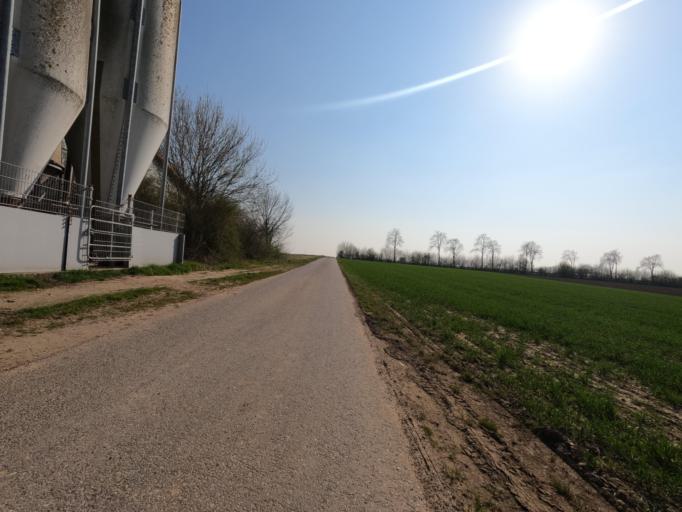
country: DE
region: North Rhine-Westphalia
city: Erkelenz
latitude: 51.0921
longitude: 6.2712
